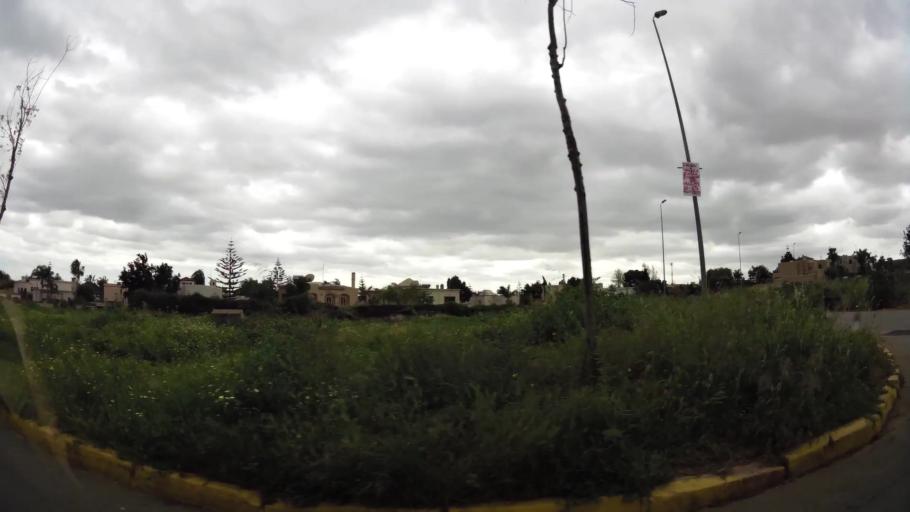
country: MA
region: Grand Casablanca
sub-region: Casablanca
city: Casablanca
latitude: 33.5316
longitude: -7.6335
